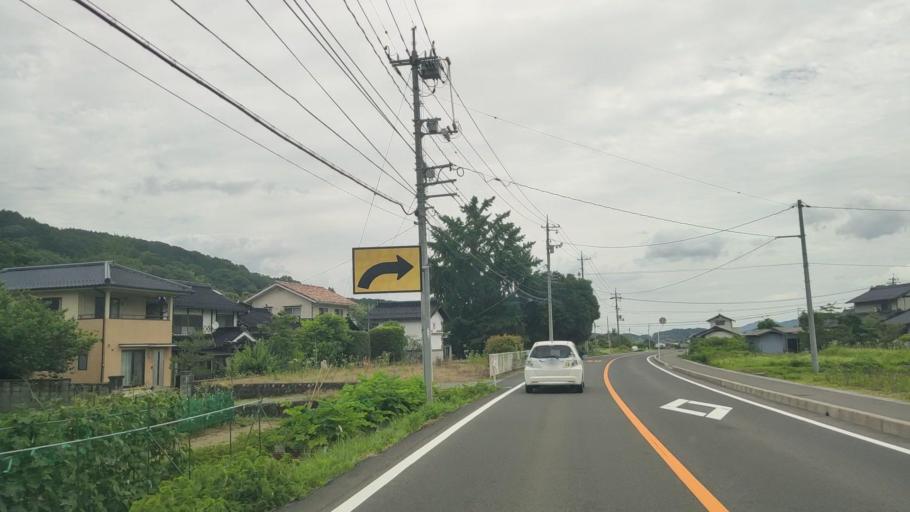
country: JP
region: Okayama
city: Tsuyama
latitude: 35.0619
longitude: 133.8813
